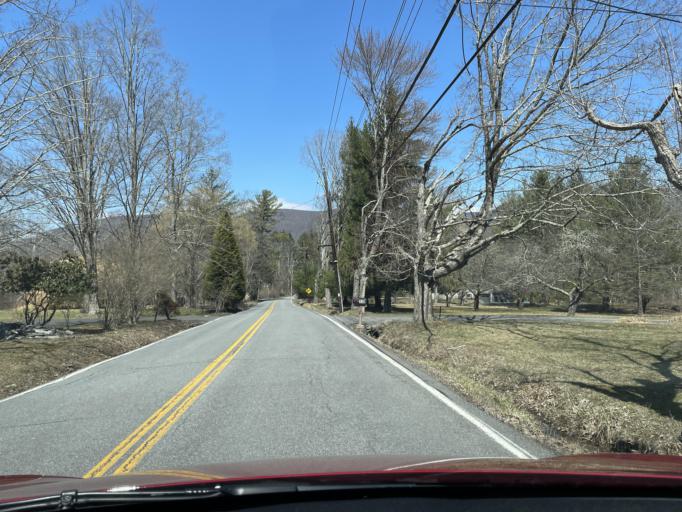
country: US
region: New York
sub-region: Ulster County
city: Woodstock
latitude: 42.0323
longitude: -74.1246
